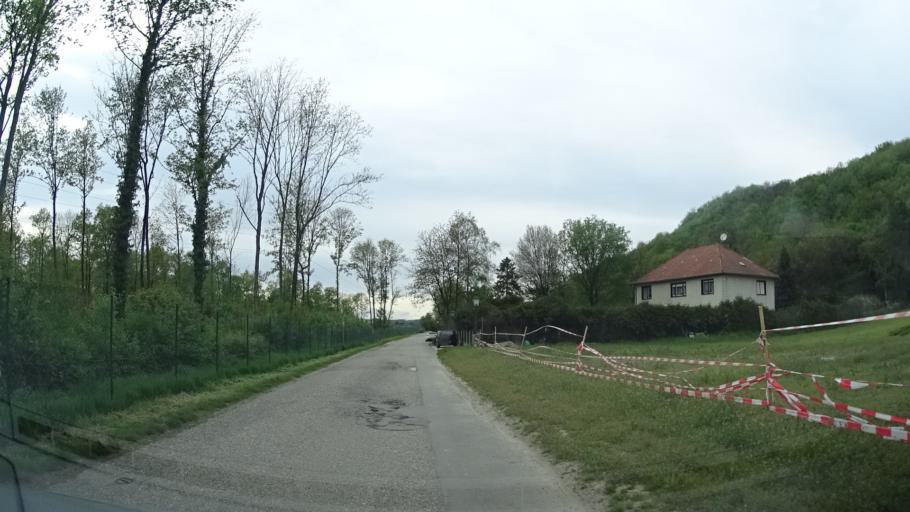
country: AT
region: Lower Austria
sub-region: Politischer Bezirk Korneuburg
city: Leobendorf
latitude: 48.3703
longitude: 16.3021
